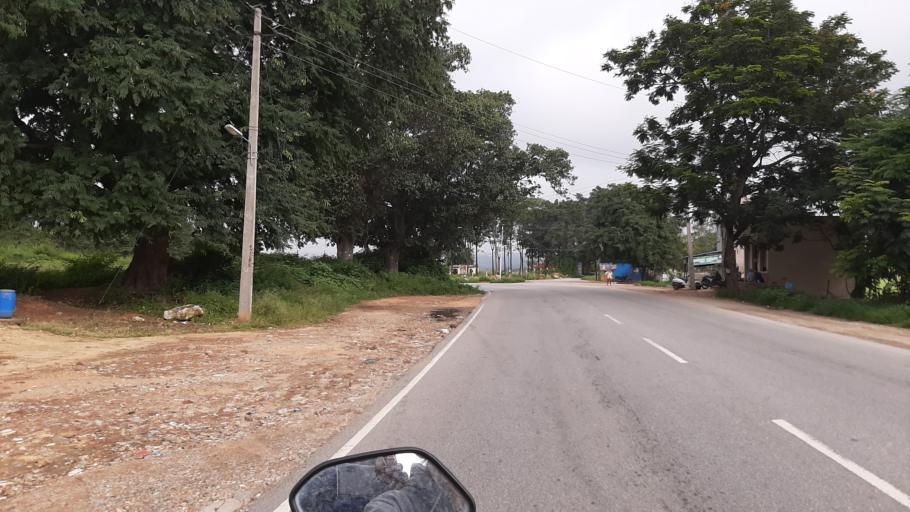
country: IN
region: Karnataka
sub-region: Bangalore Rural
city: Nelamangala
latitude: 12.9736
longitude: 77.3743
